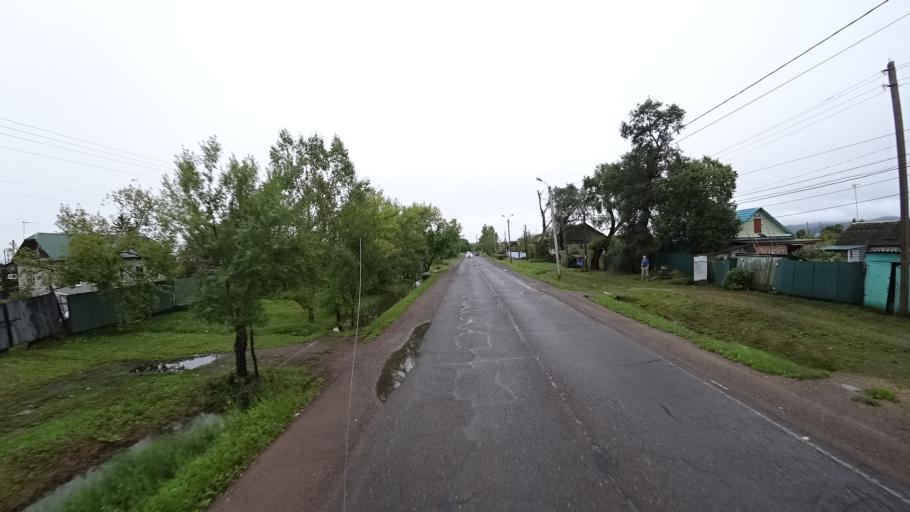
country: RU
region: Primorskiy
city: Monastyrishche
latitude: 44.1993
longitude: 132.4605
